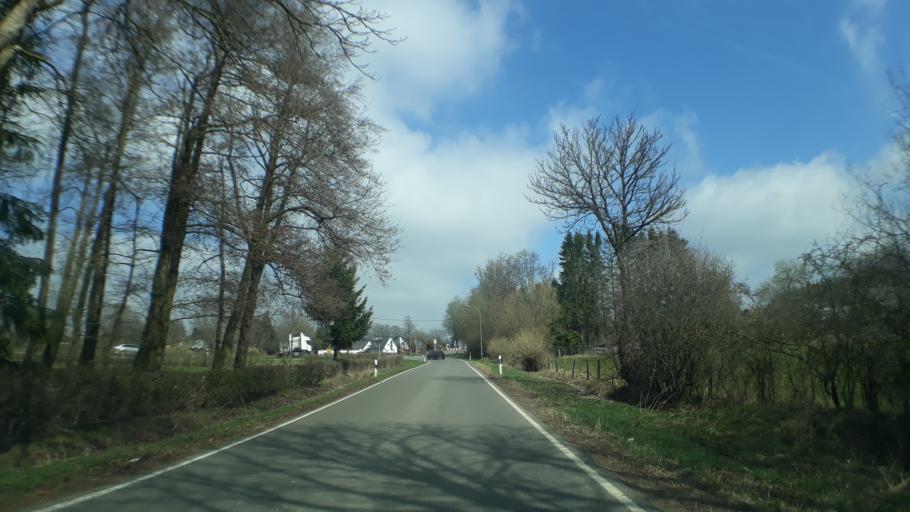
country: DE
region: North Rhine-Westphalia
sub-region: Regierungsbezirk Koln
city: Monschau
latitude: 50.5673
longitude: 6.2611
